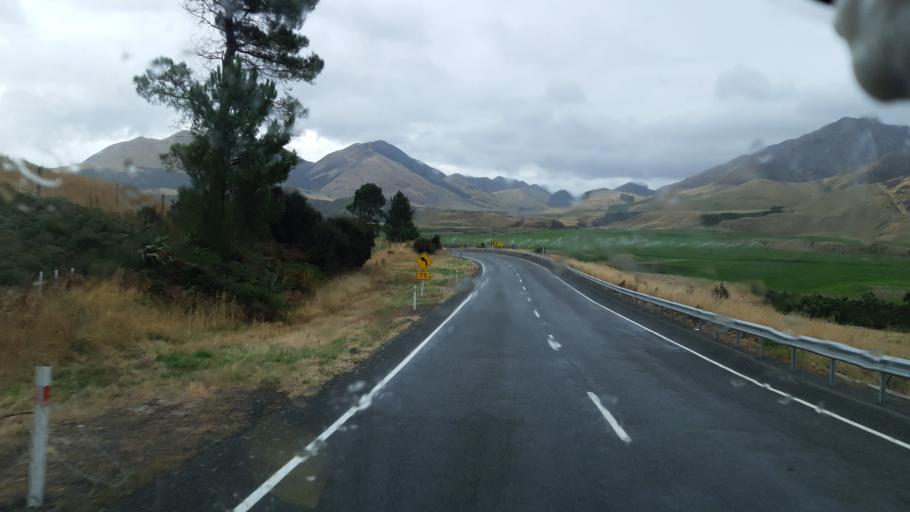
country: NZ
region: Canterbury
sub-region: Hurunui District
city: Amberley
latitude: -42.6383
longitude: 172.7706
